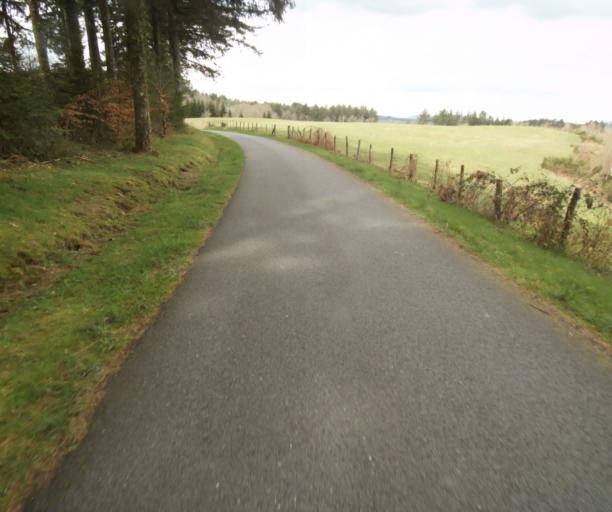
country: FR
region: Limousin
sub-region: Departement de la Correze
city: Egletons
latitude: 45.3393
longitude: 1.9759
